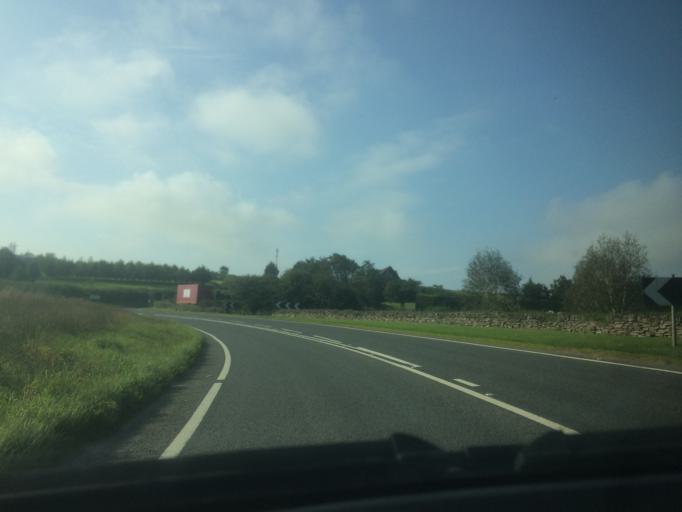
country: GB
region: England
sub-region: Cornwall
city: Saltash
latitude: 50.4302
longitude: -4.2587
